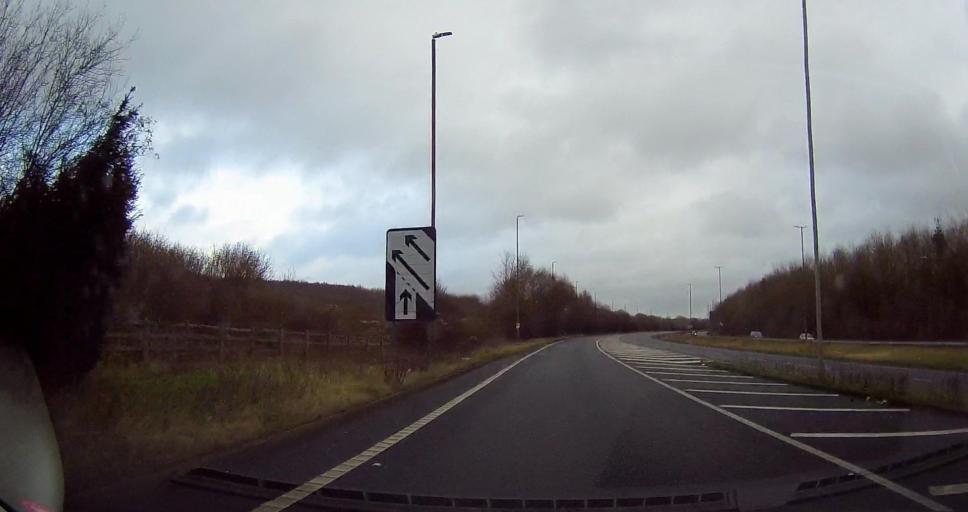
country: GB
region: England
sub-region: Medway
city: Cuxton
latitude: 51.4015
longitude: 0.4467
